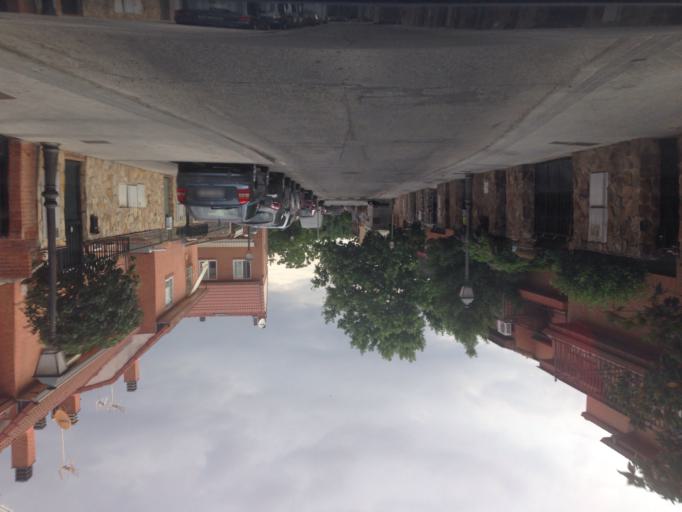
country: ES
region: Madrid
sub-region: Provincia de Madrid
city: Daganzo de Arriba
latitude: 40.5468
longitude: -3.4555
